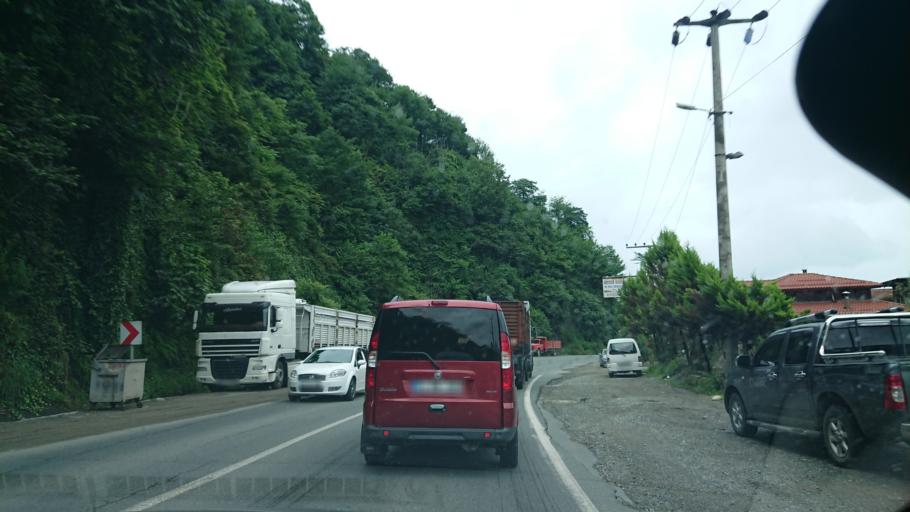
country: TR
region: Rize
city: Gundogdu
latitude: 41.0357
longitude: 40.5790
